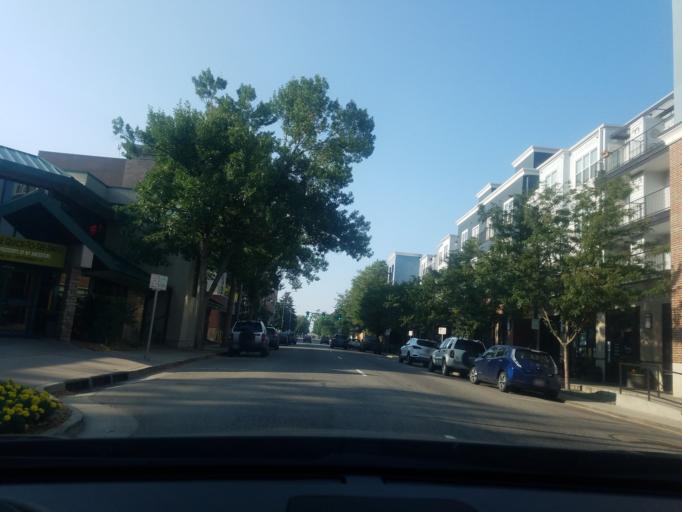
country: US
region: Colorado
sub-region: Larimer County
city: Loveland
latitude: 40.3966
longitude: -105.0732
